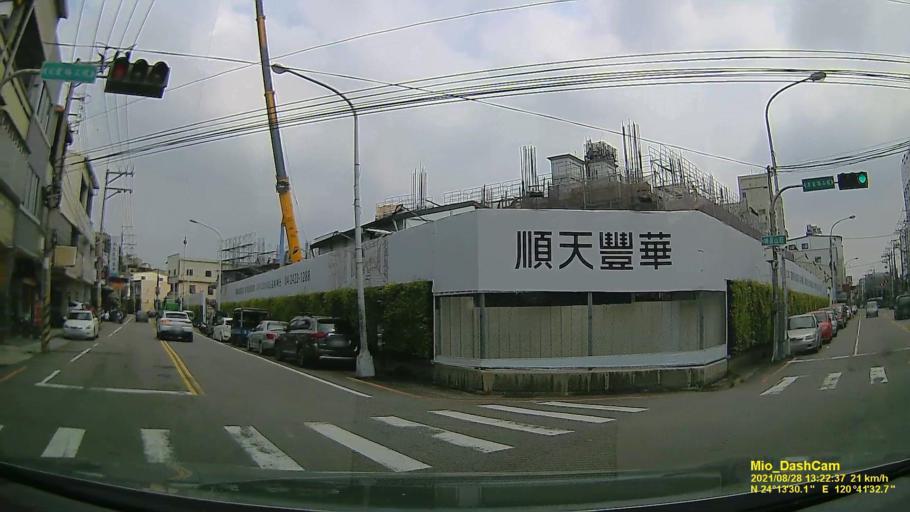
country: TW
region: Taiwan
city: Fengyuan
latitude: 24.2250
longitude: 120.6924
